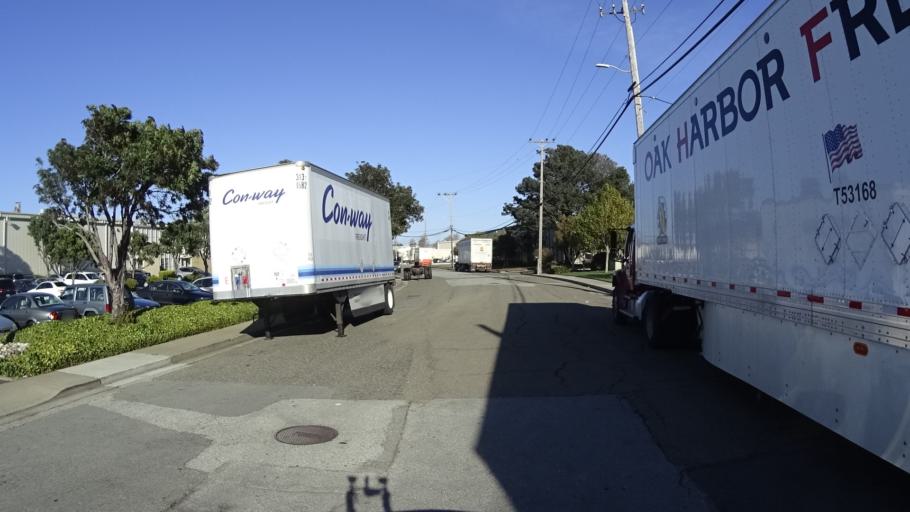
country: US
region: California
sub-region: San Mateo County
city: South San Francisco
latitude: 37.6444
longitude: -122.3973
